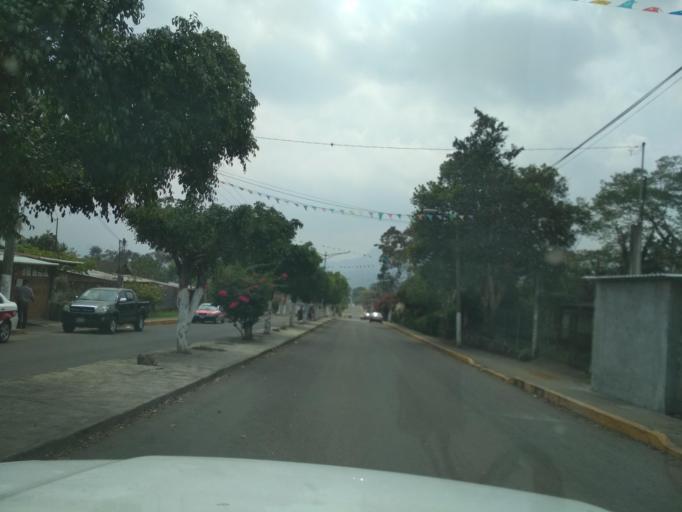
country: MX
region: Veracruz
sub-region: Cordoba
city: Fredepo
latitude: 18.8541
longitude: -96.9823
